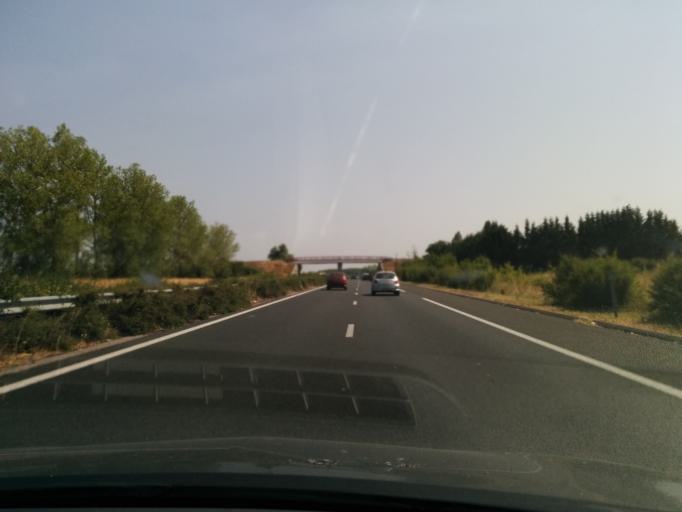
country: FR
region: Midi-Pyrenees
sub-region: Departement du Tarn
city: Marssac-sur-Tarn
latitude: 43.8915
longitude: 2.0225
